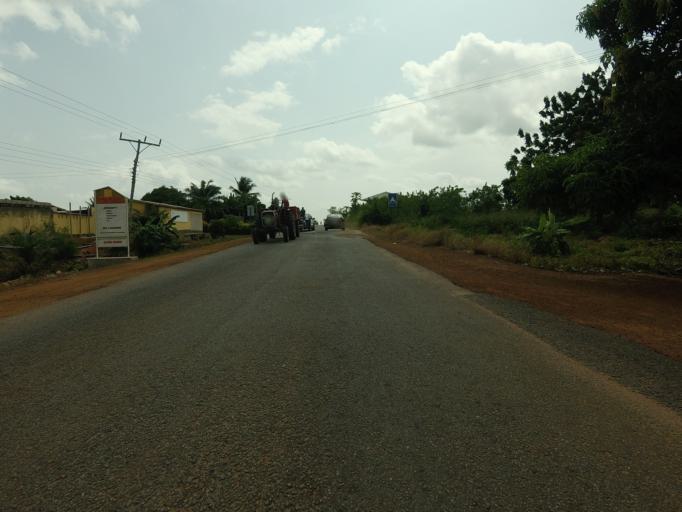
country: TG
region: Maritime
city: Lome
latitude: 6.2255
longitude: 1.0245
